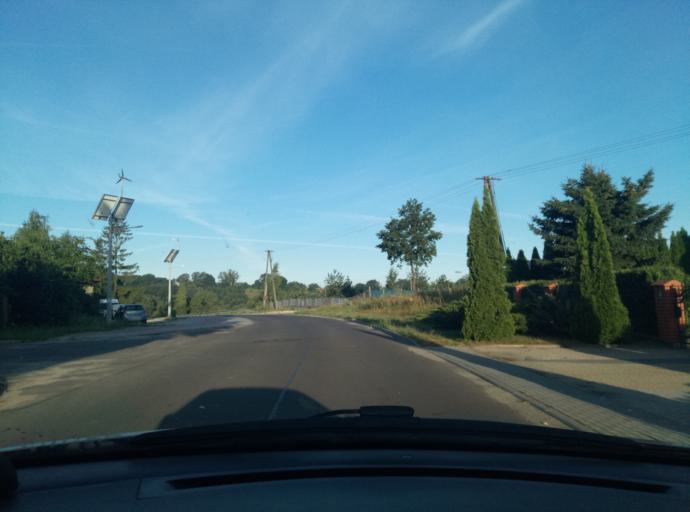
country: PL
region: Kujawsko-Pomorskie
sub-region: Powiat brodnicki
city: Jablonowo Pomorskie
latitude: 53.3900
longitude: 19.1459
